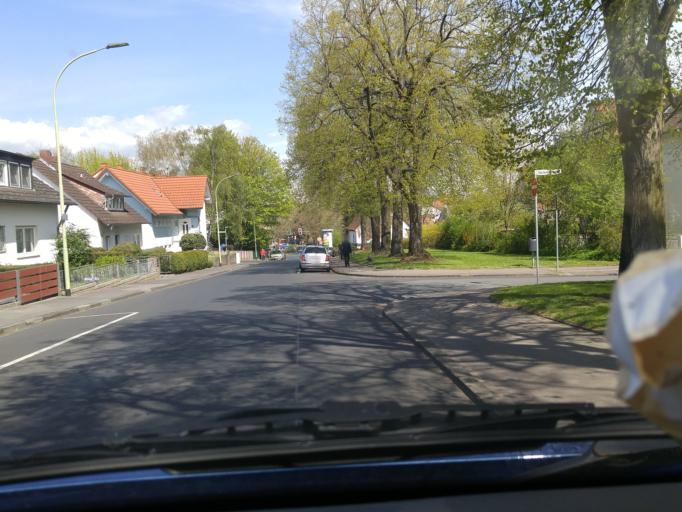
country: DE
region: Hesse
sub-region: Regierungsbezirk Darmstadt
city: Friedberg
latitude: 50.3327
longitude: 8.7469
